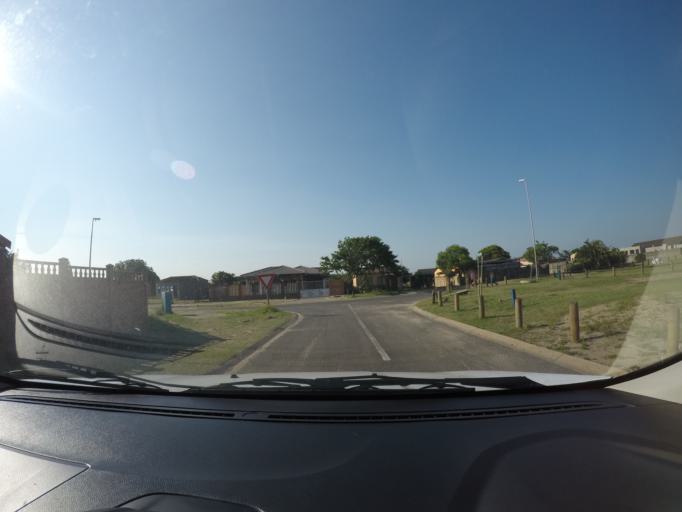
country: ZA
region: KwaZulu-Natal
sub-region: uThungulu District Municipality
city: Richards Bay
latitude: -28.7156
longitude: 32.0353
